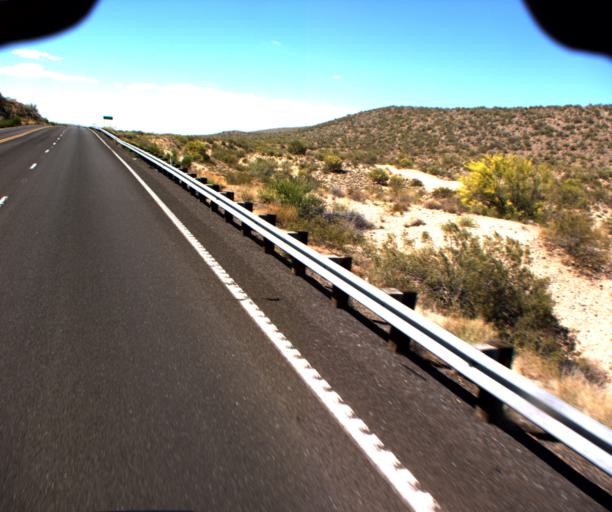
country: US
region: Arizona
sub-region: Mohave County
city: Kingman
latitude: 34.9331
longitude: -113.6608
